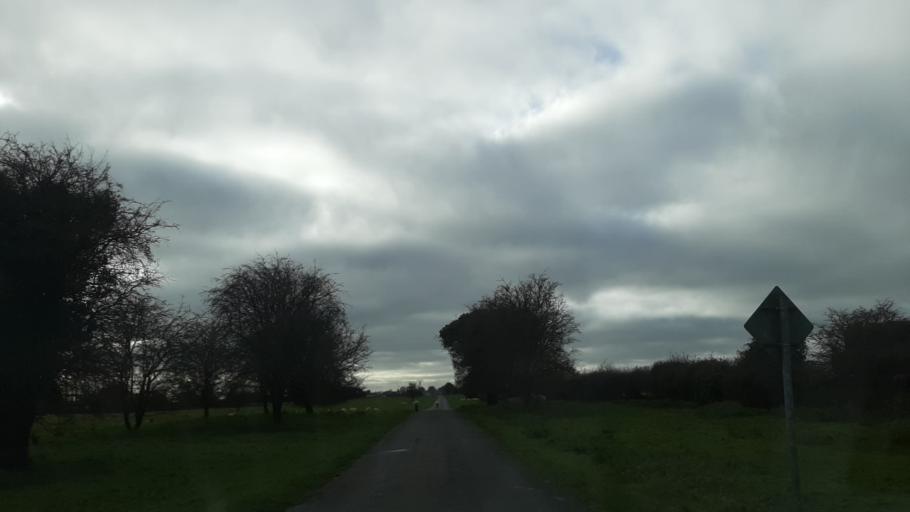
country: IE
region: Leinster
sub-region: Kildare
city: Kildare
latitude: 53.1772
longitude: -6.8966
